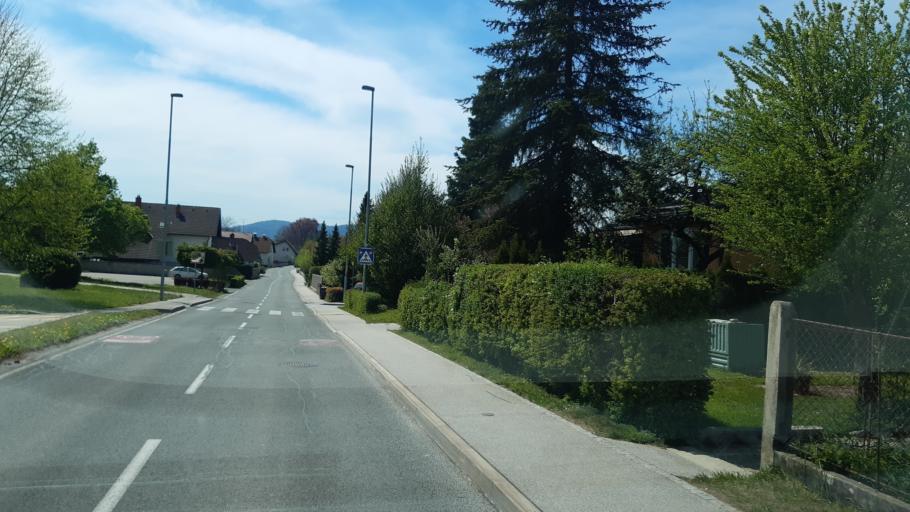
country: SI
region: Domzale
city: Radomlje
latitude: 46.1751
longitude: 14.6164
